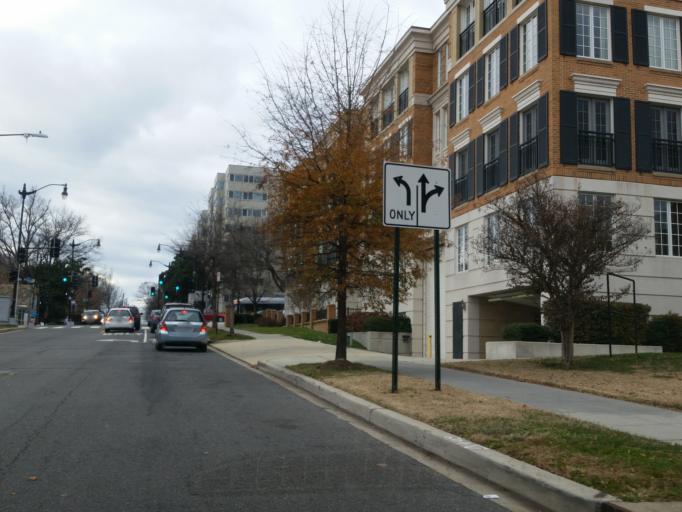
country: US
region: Maryland
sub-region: Montgomery County
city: Friendship Village
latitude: 38.9226
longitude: -77.0720
